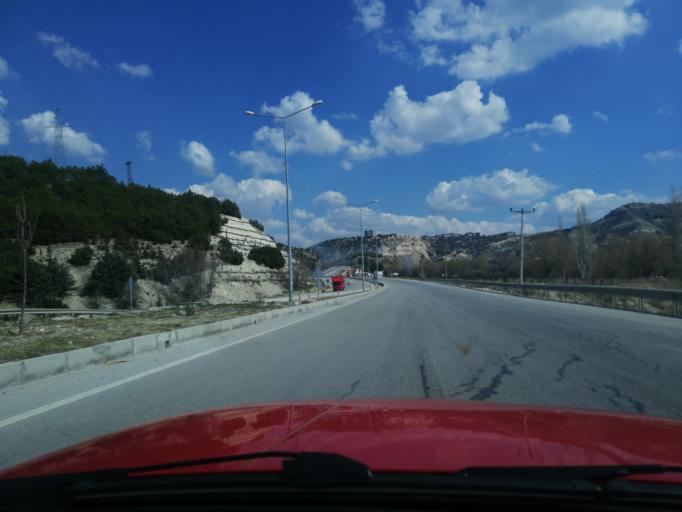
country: TR
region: Burdur
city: Burdur
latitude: 37.6994
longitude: 30.3209
